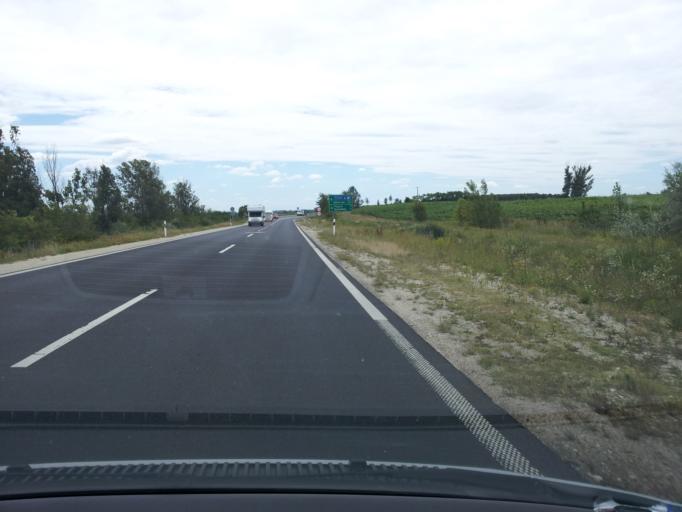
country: HU
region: Fejer
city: Lepseny
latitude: 47.0207
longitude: 18.1835
